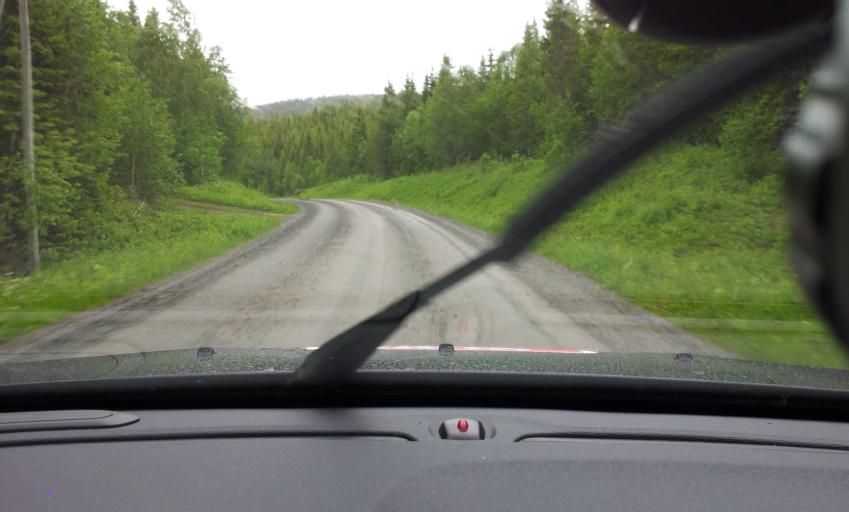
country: SE
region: Jaemtland
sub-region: Are Kommun
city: Are
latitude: 63.4756
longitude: 12.8090
